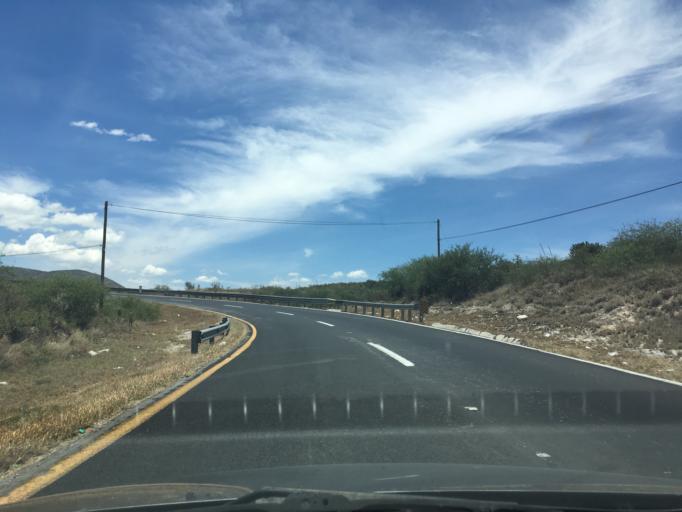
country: MX
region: Hidalgo
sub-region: Ixmiquilpan
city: Taxadho
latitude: 20.4137
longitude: -99.1329
